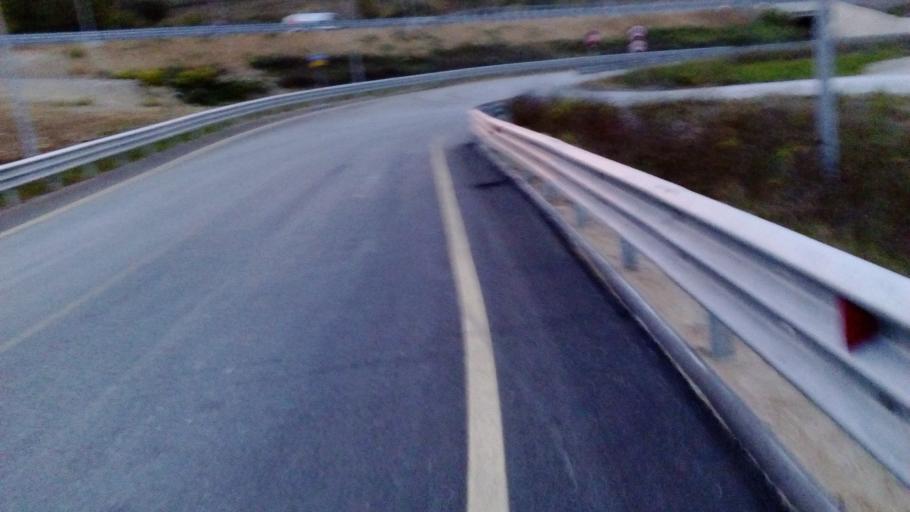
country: IT
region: Tuscany
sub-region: Provincia di Grosseto
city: Civitella Marittima
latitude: 43.0280
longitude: 11.2773
